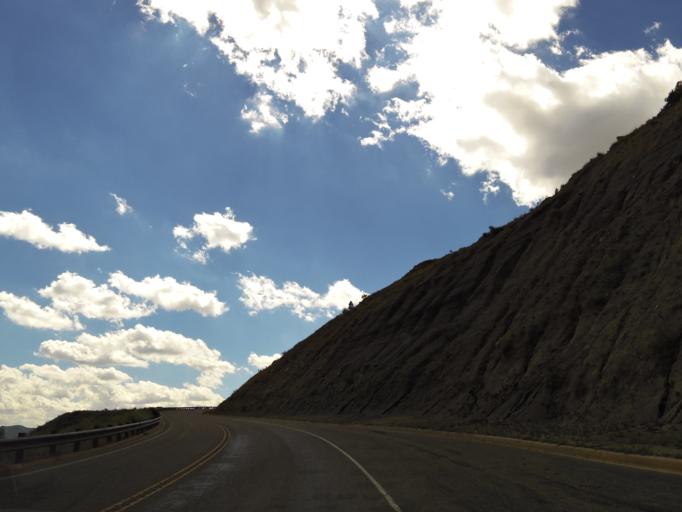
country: US
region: Colorado
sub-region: Montezuma County
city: Mancos
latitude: 37.3094
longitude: -108.4145
